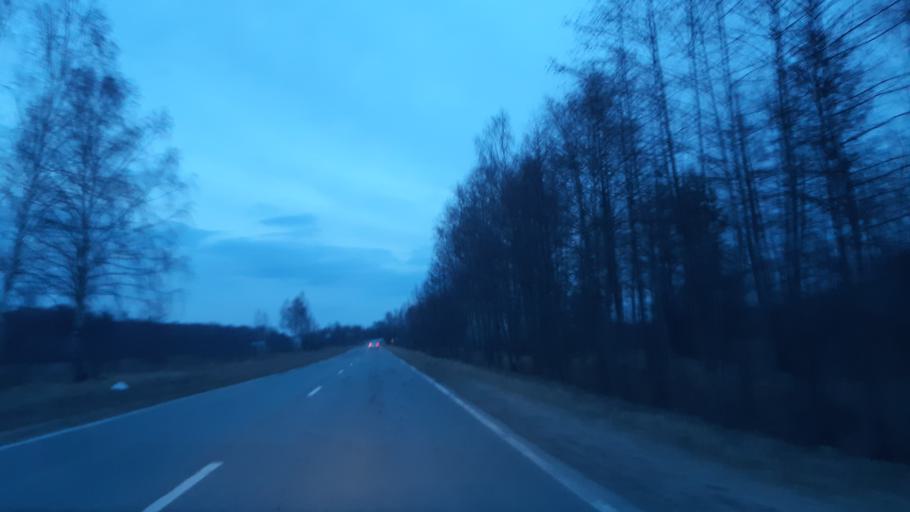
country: RU
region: Vladimir
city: Luknovo
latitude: 56.1830
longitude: 42.0140
